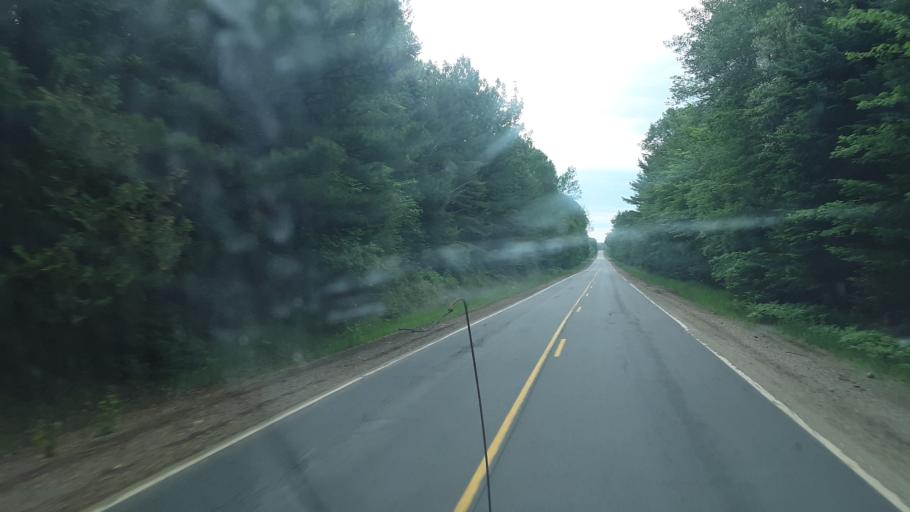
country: US
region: Maine
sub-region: Penobscot County
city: Medway
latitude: 45.6538
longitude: -68.2704
